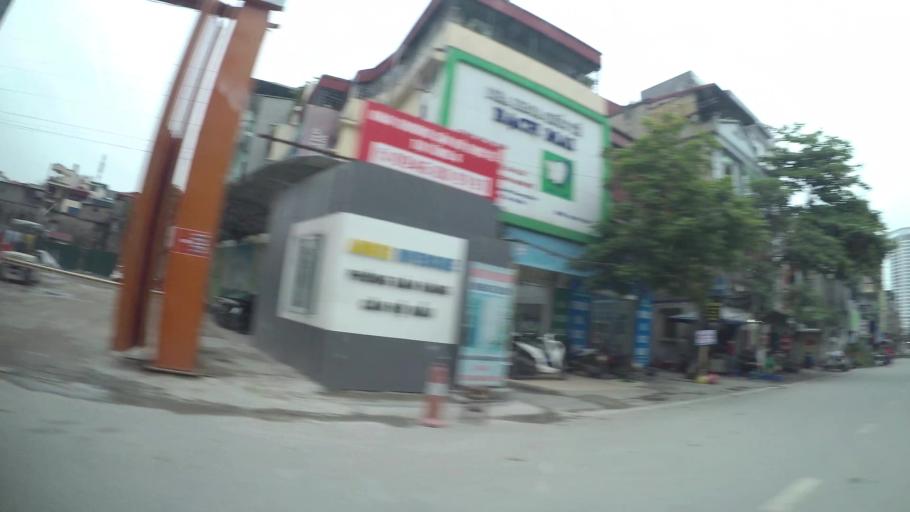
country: VN
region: Ha Noi
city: Hai BaTrung
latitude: 20.9970
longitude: 105.8711
